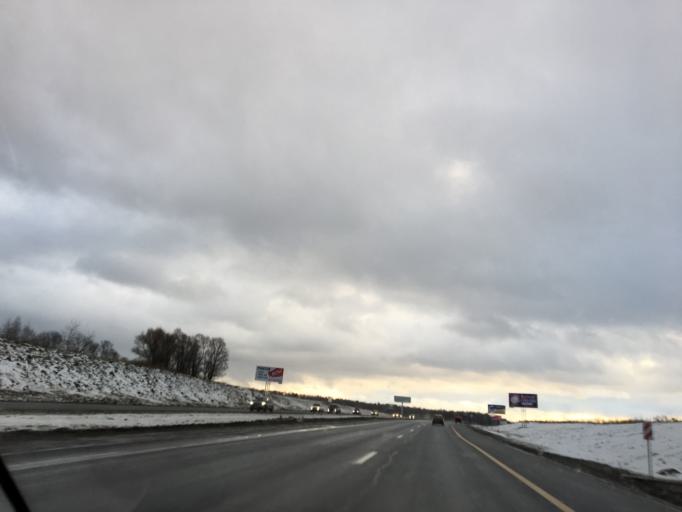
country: RU
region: Moskovskaya
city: Danki
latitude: 54.9440
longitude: 37.5301
